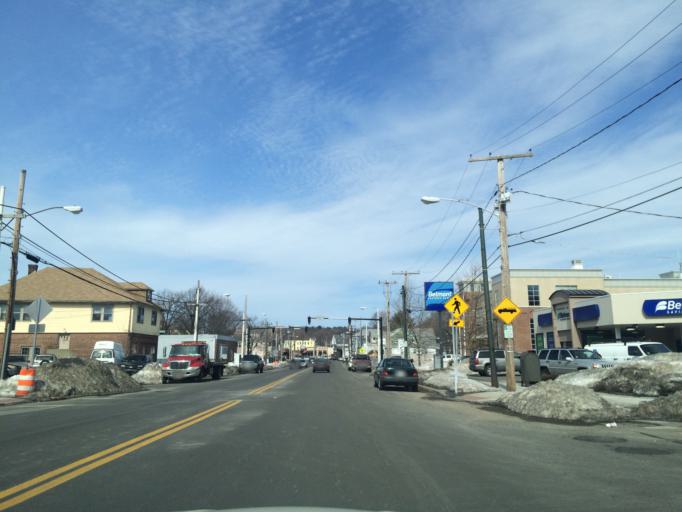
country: US
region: Massachusetts
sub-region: Middlesex County
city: Watertown
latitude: 42.3834
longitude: -71.1810
